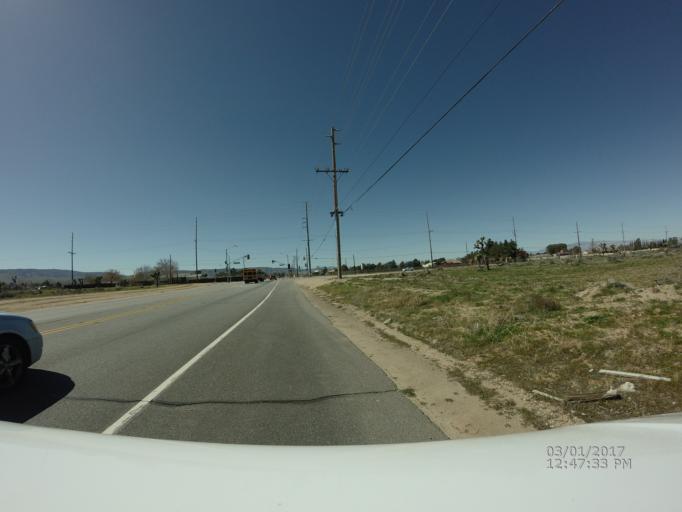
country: US
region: California
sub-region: Los Angeles County
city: Quartz Hill
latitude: 34.6458
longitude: -118.1646
